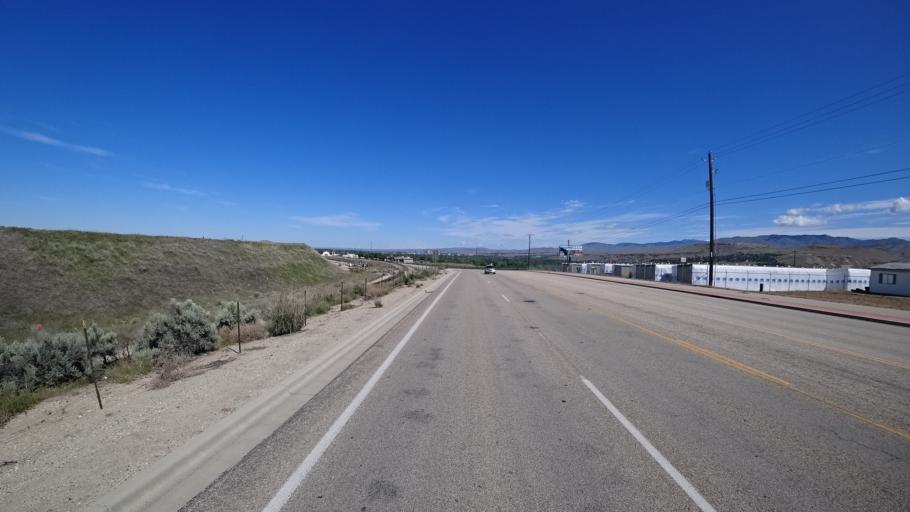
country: US
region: Idaho
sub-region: Ada County
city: Boise
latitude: 43.5559
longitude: -116.1632
